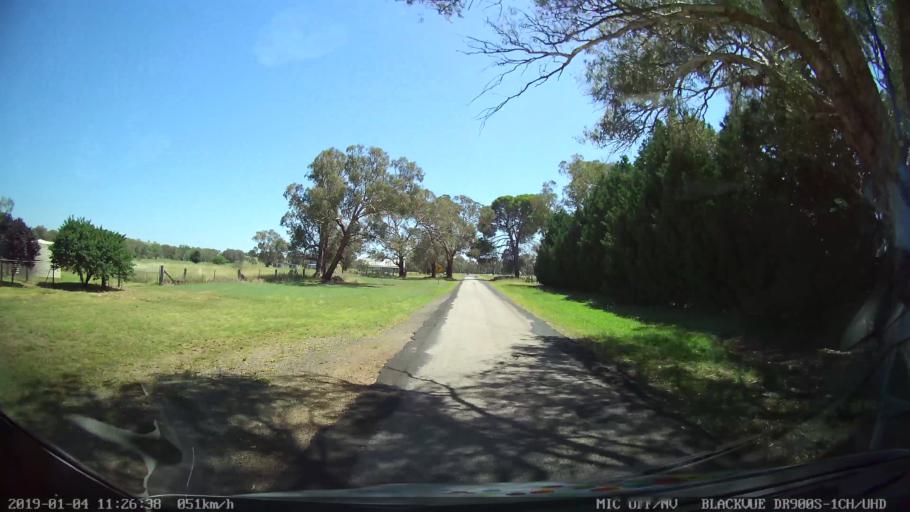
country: AU
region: New South Wales
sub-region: Cabonne
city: Molong
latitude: -33.1140
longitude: 148.7567
